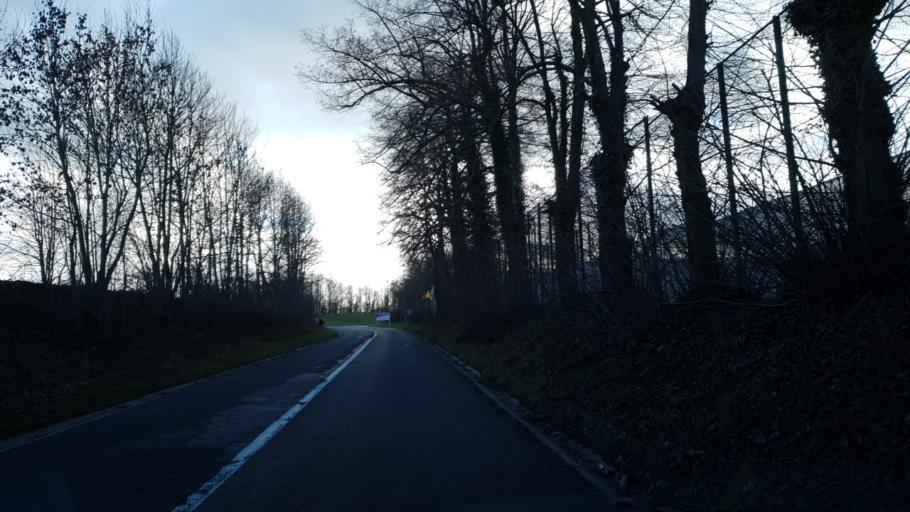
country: BE
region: Flanders
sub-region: Provincie Vlaams-Brabant
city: Kortenberg
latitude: 50.8690
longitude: 4.5796
